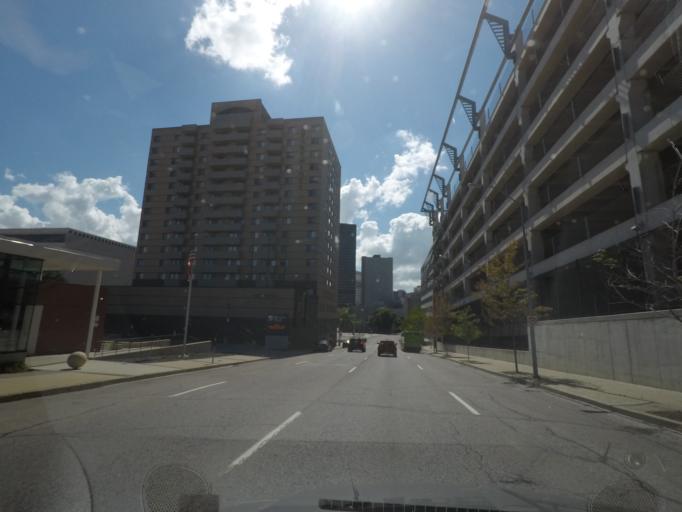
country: US
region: Iowa
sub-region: Polk County
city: Des Moines
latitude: 41.5914
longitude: -93.6269
